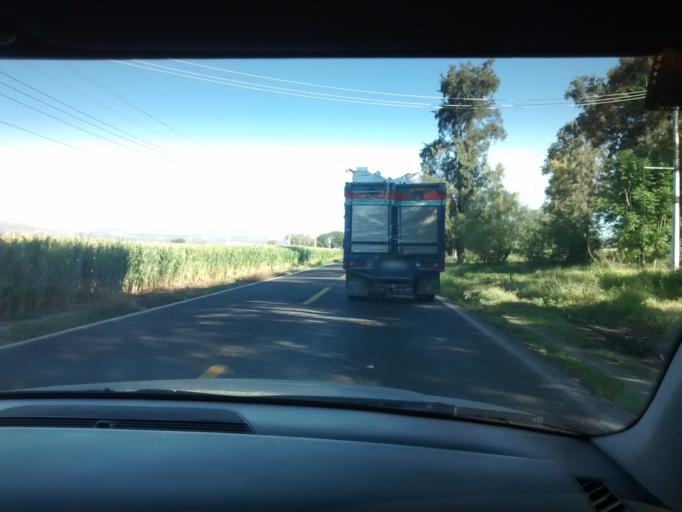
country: MX
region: Puebla
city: San Bartolo Teontepec
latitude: 18.5347
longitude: -97.5278
